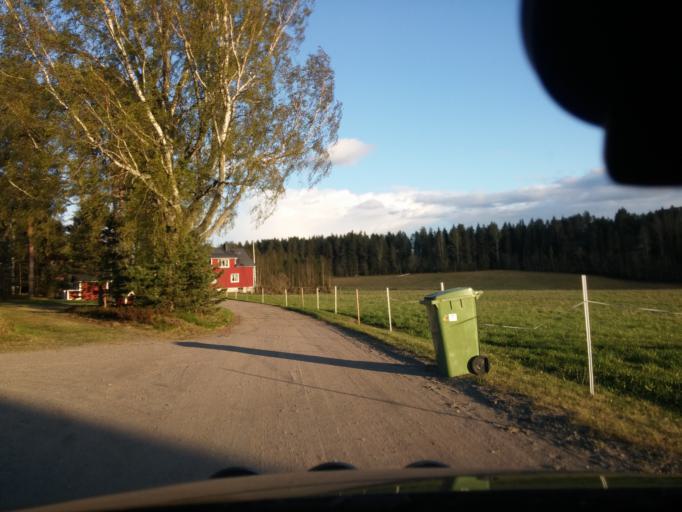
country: SE
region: Gaevleborg
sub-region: Bollnas Kommun
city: Kilafors
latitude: 61.3742
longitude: 16.6214
